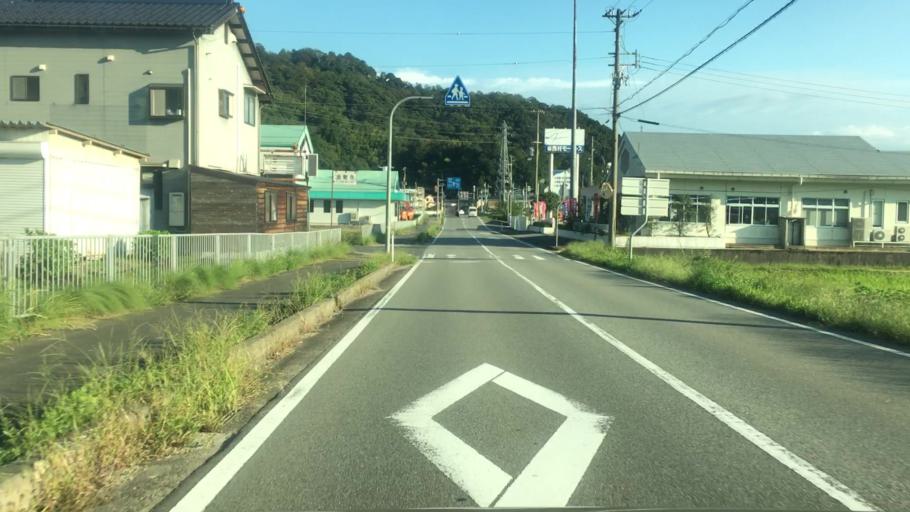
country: JP
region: Hyogo
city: Toyooka
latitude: 35.5603
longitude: 134.8234
